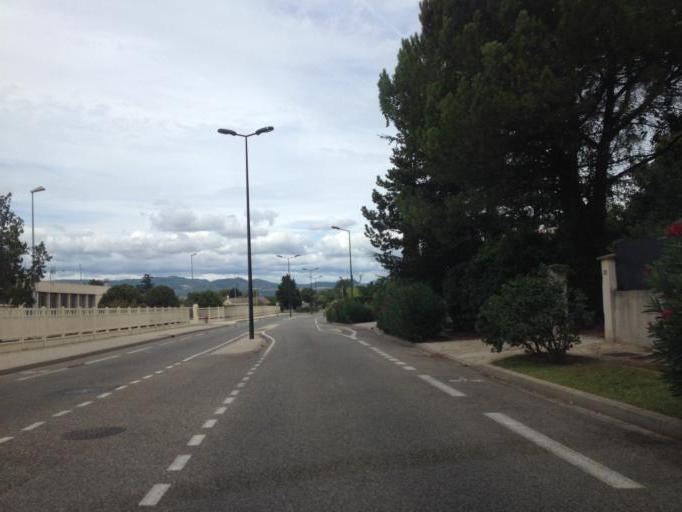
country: FR
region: Rhone-Alpes
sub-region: Departement de la Drome
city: Montelimar
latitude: 44.5438
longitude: 4.7574
